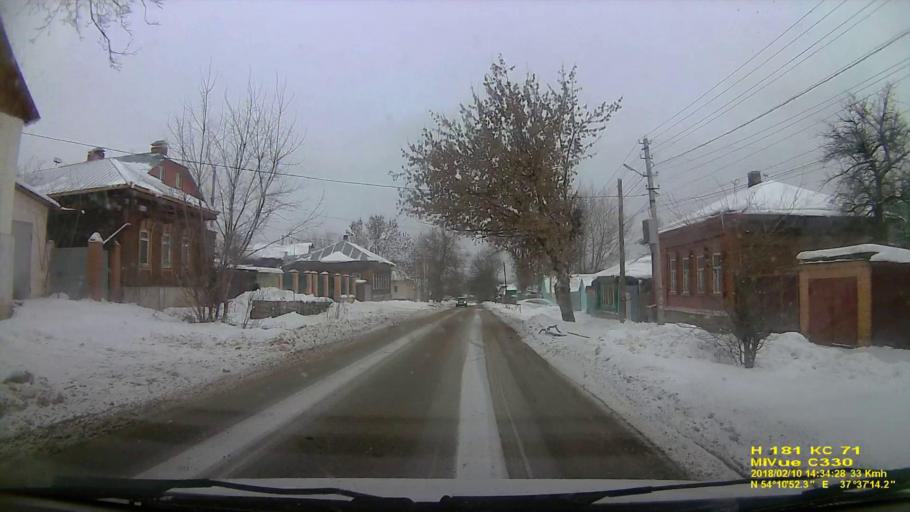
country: RU
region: Tula
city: Tula
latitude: 54.1812
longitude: 37.6206
